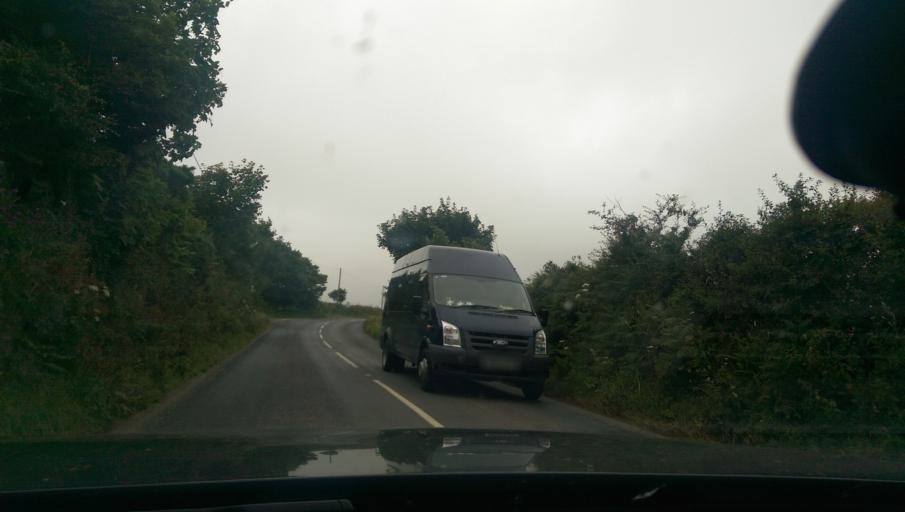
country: GB
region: England
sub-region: Cornwall
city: St. Buryan
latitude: 50.0910
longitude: -5.6310
